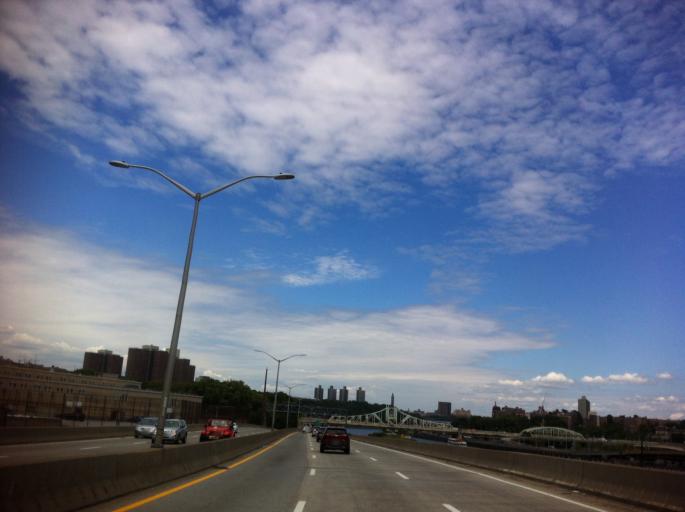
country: US
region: New Jersey
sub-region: Bergen County
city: Edgewater
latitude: 40.8222
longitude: -73.9344
